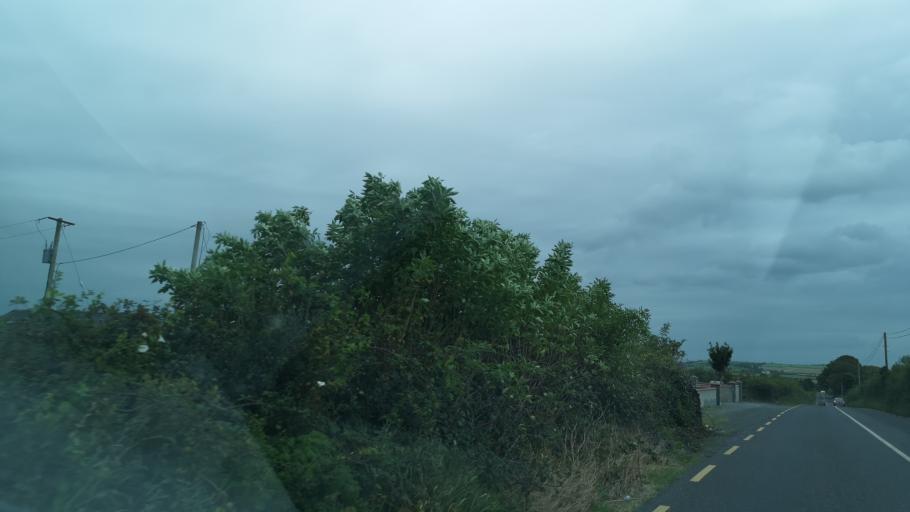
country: IE
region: Leinster
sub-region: Uibh Fhaili
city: Banagher
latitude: 53.2076
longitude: -7.9201
